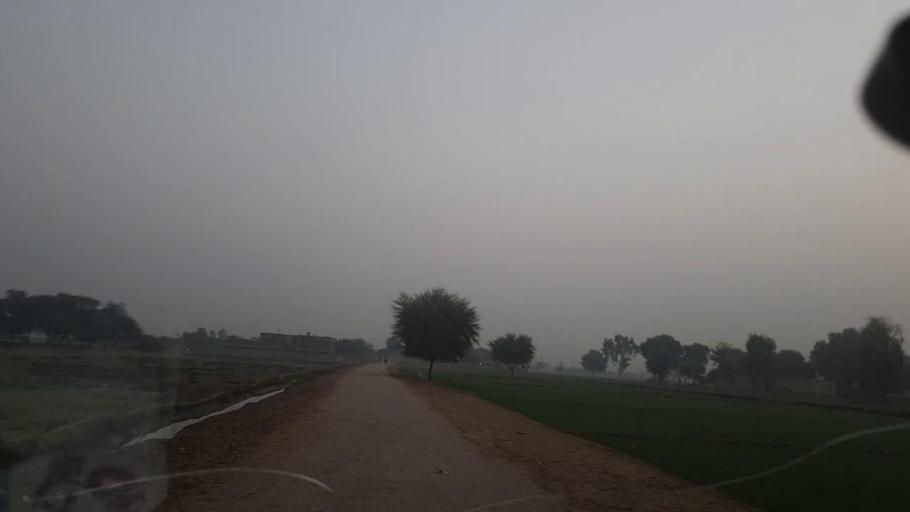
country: PK
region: Sindh
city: Hingorja
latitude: 27.2233
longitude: 68.4276
